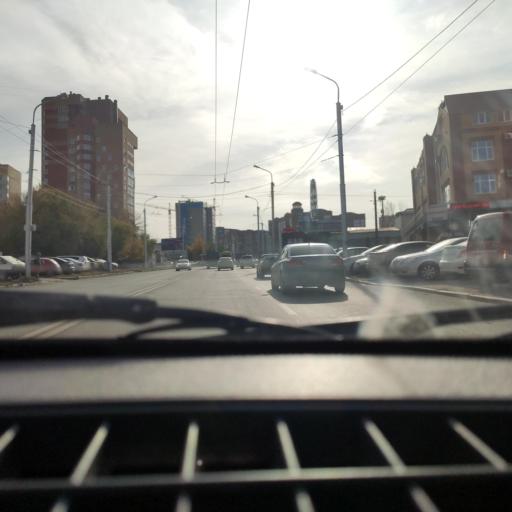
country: RU
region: Bashkortostan
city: Ufa
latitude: 54.7164
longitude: 55.9936
